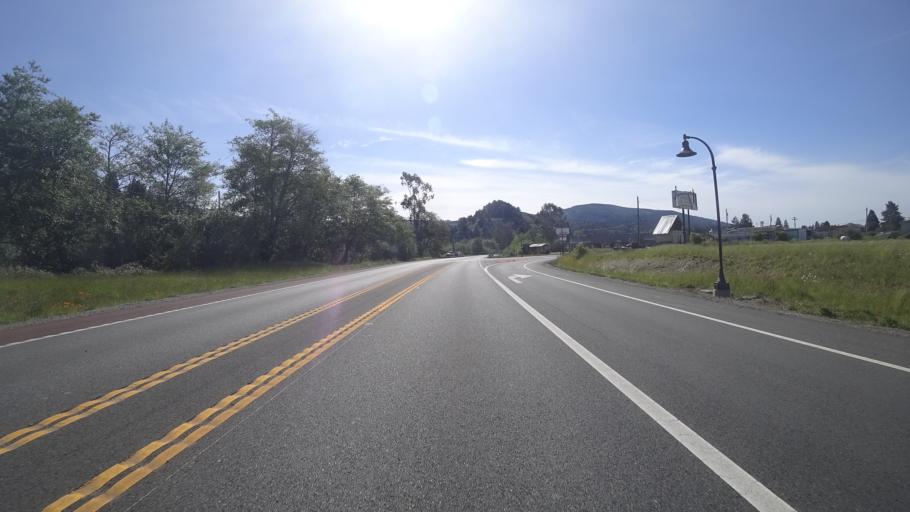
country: US
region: Oregon
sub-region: Curry County
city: Harbor
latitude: 41.9304
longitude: -124.1469
